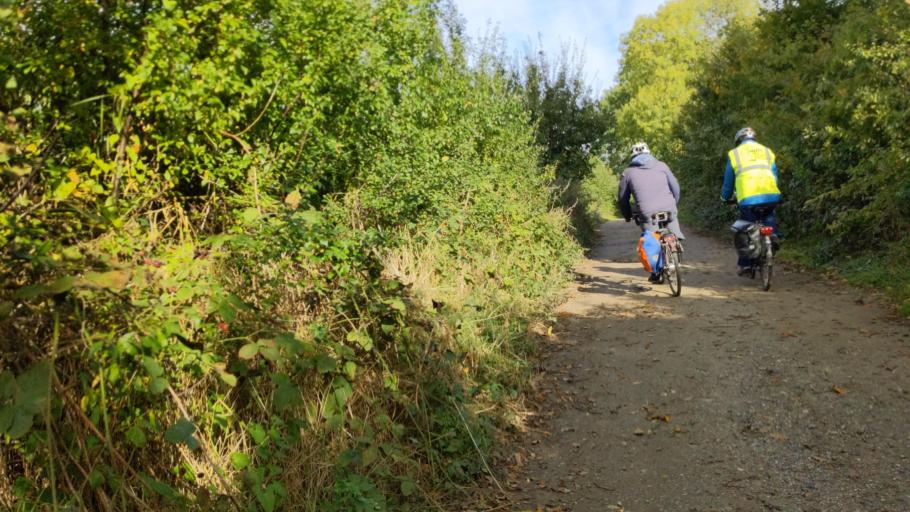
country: DE
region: Schleswig-Holstein
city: Zarpen
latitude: 53.8623
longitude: 10.5142
